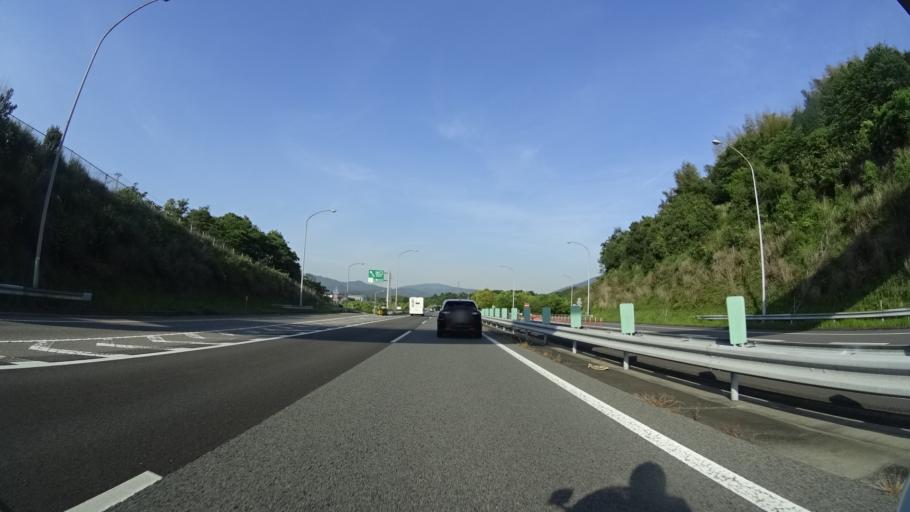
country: JP
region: Ehime
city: Kawanoecho
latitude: 33.9779
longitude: 133.5741
